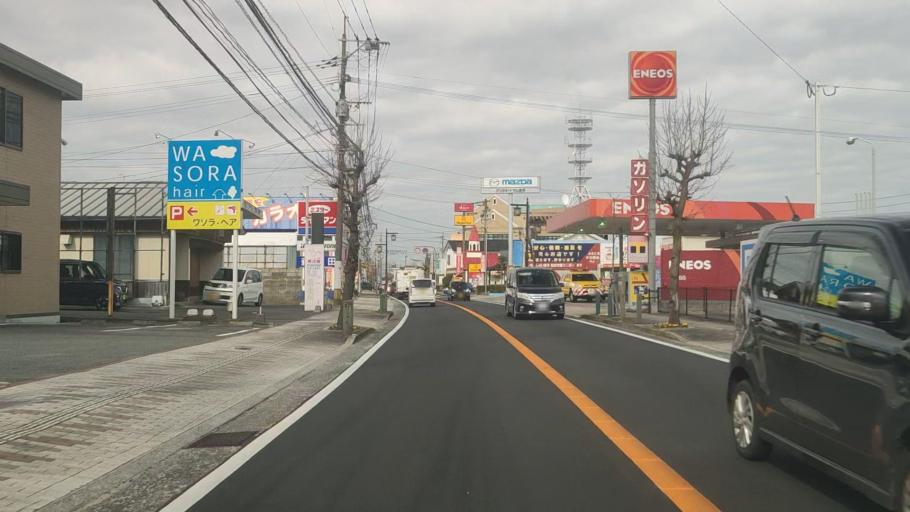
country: JP
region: Nagasaki
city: Shimabara
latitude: 32.7960
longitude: 130.3676
